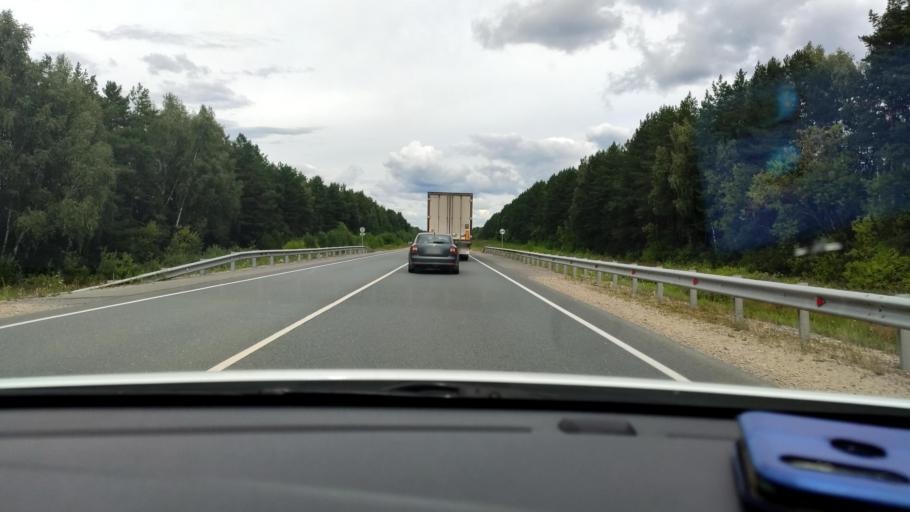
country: RU
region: Mariy-El
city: Pomary
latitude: 55.9867
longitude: 48.3777
